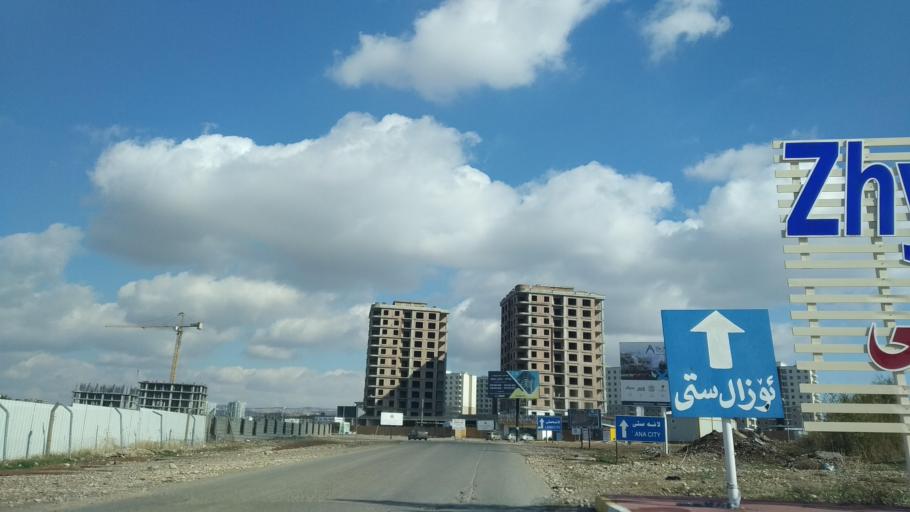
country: IQ
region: Arbil
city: Erbil
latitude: 36.2127
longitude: 44.1363
